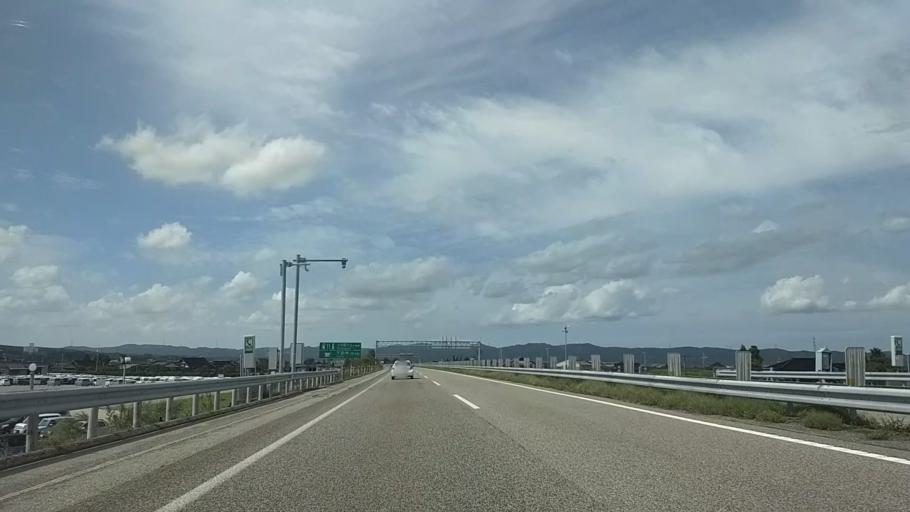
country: JP
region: Toyama
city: Nanto-shi
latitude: 36.6314
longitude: 136.9029
